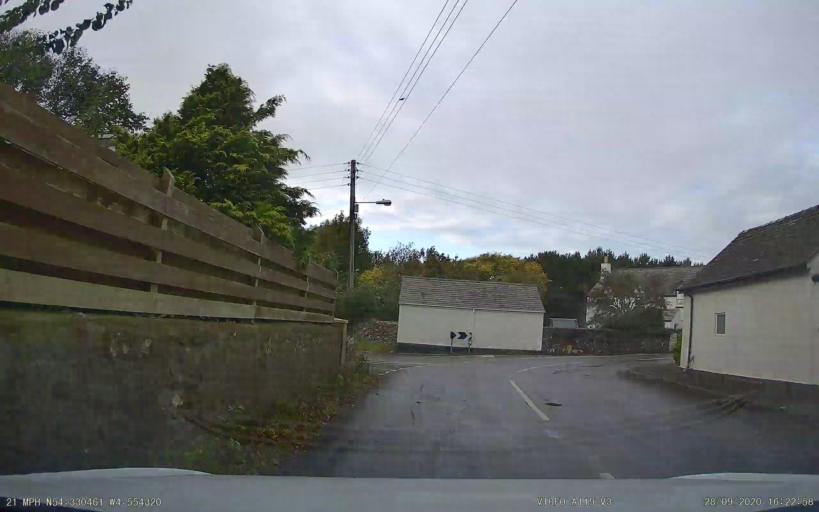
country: IM
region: Ramsey
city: Ramsey
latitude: 54.3305
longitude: -4.5544
